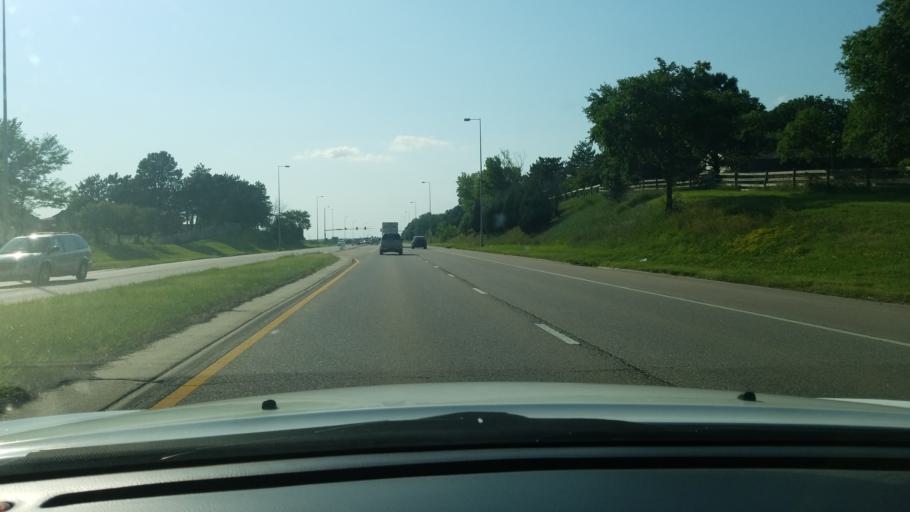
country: US
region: Nebraska
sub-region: Lancaster County
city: Lincoln
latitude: 40.7499
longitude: -96.6321
